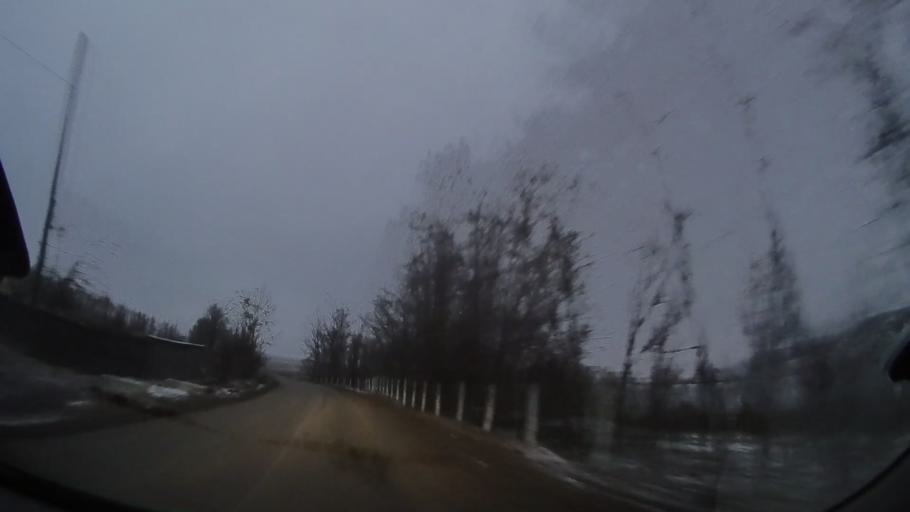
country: RO
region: Vaslui
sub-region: Comuna Vutcani
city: Vutcani
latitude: 46.4184
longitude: 27.9973
